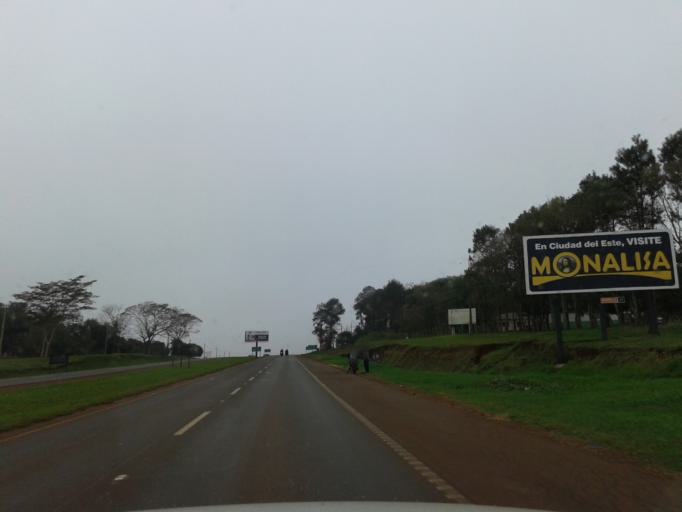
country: PY
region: Alto Parana
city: Colonia Yguazu
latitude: -25.4860
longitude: -54.8750
